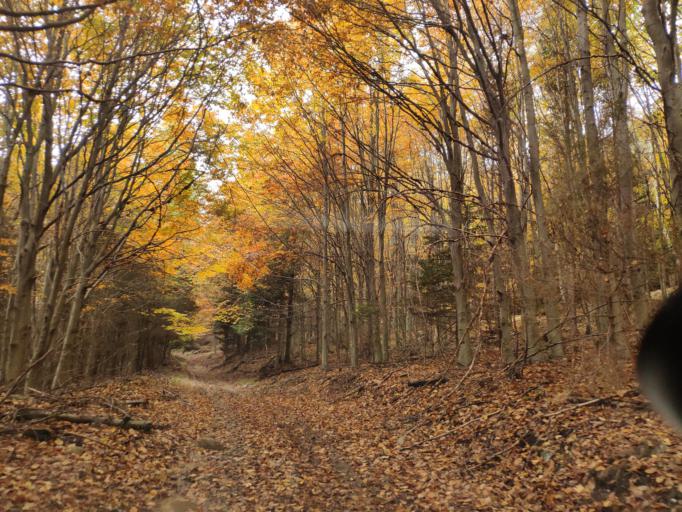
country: SK
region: Kosicky
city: Medzev
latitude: 48.7502
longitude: 20.9820
